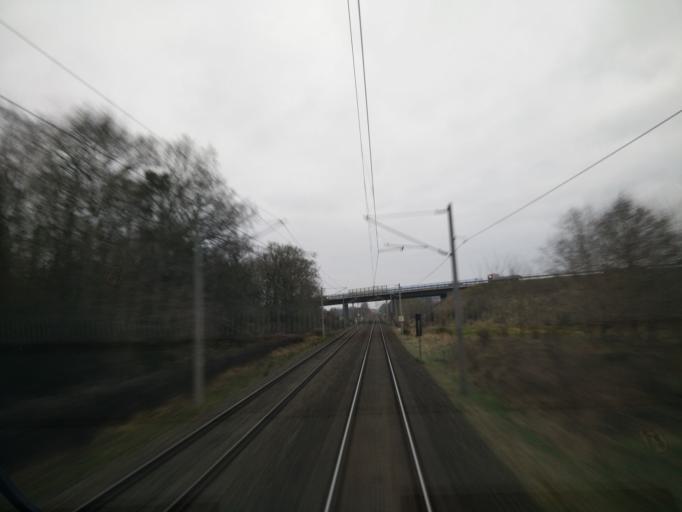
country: DE
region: Brandenburg
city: Karstadt
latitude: 53.1461
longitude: 11.7407
